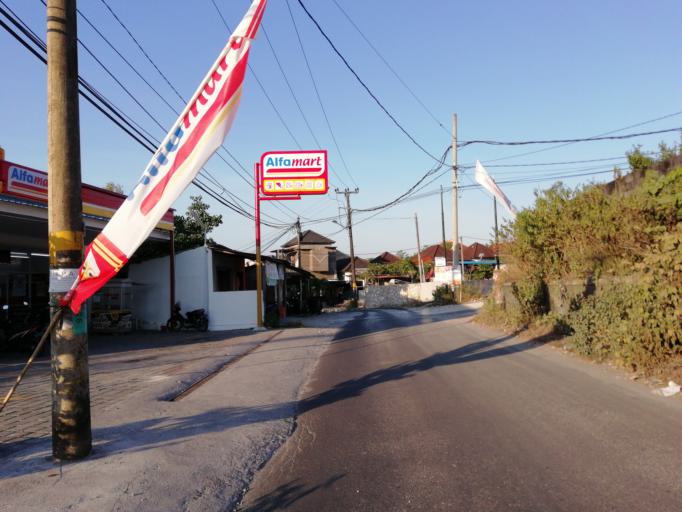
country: ID
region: Bali
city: Bualu
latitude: -8.8002
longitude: 115.1953
